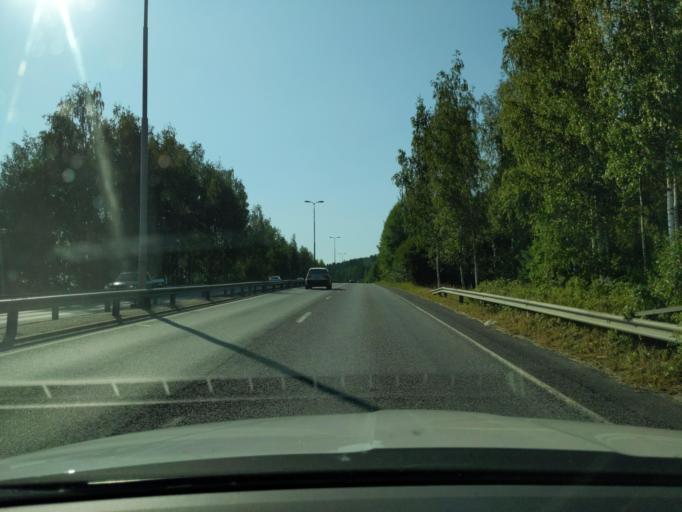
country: FI
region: Paijanne Tavastia
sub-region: Lahti
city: Lahti
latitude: 60.9751
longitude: 25.6898
